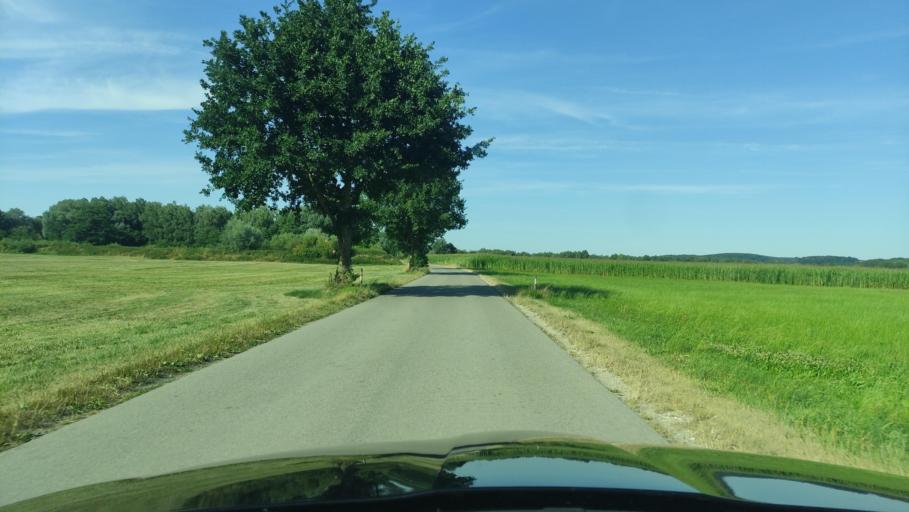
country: DE
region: Bavaria
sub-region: Swabia
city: Breitenthal
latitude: 48.2199
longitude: 10.2853
